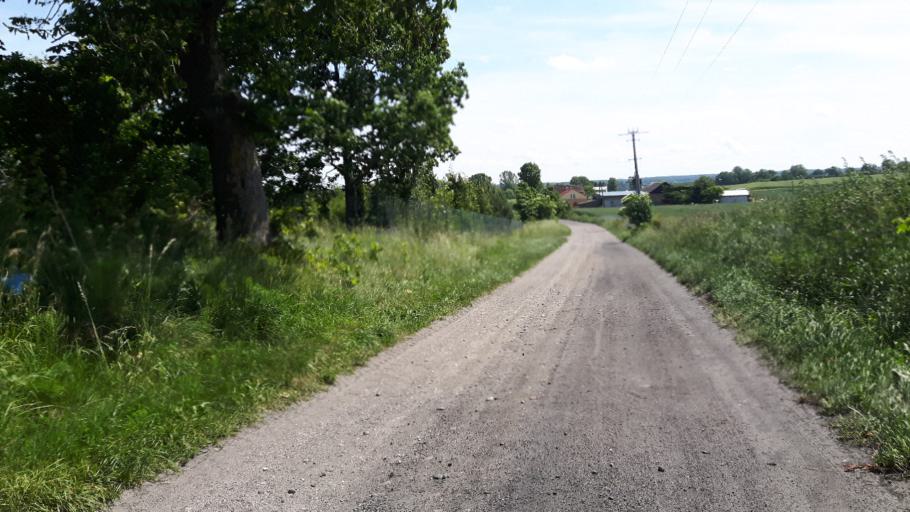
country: PL
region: Pomeranian Voivodeship
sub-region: Powiat wejherowski
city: Gniewino
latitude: 54.7286
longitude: 17.9558
